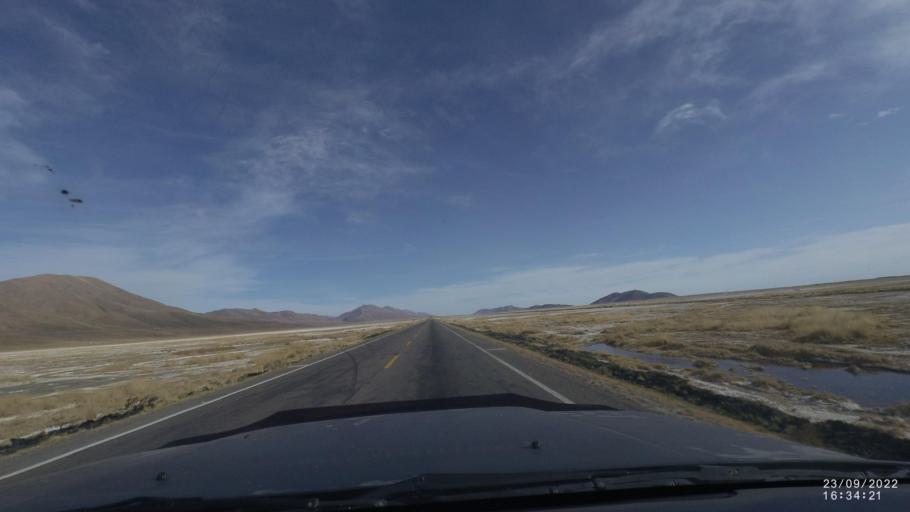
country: BO
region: Oruro
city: Machacamarca
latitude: -18.1877
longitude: -67.0146
